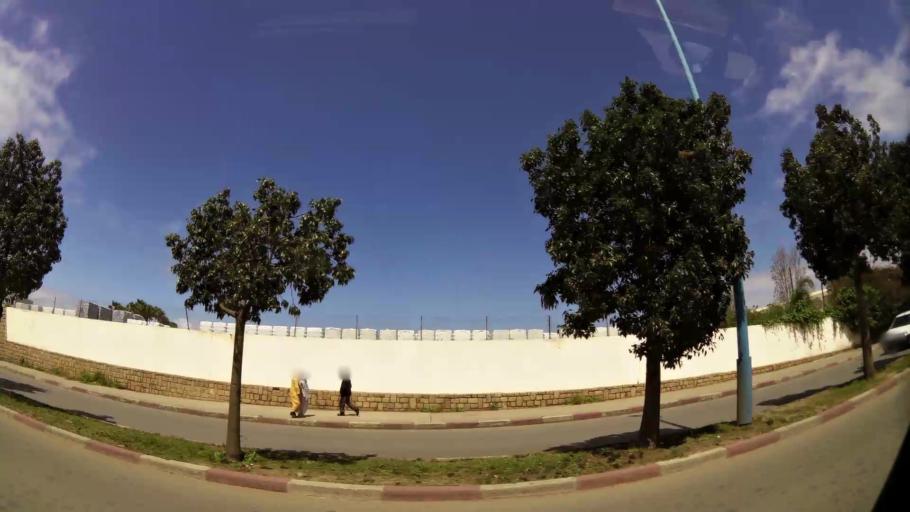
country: MA
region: Grand Casablanca
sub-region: Mediouna
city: Tit Mellil
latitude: 33.5982
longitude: -7.4969
